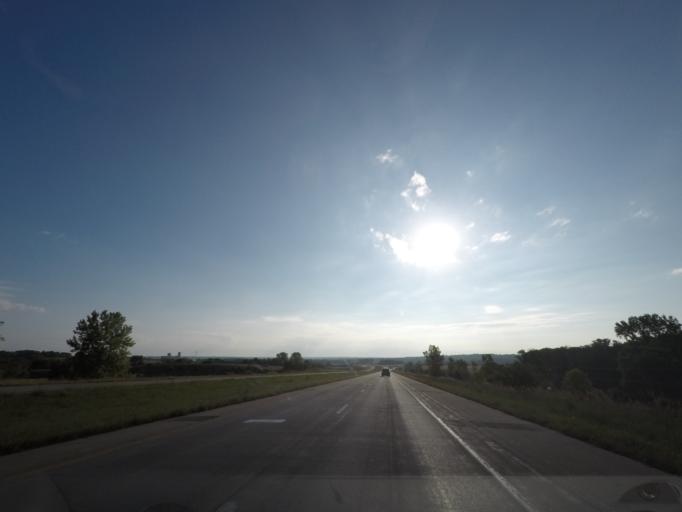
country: US
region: Iowa
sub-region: Warren County
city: Carlisle
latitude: 41.5115
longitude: -93.5384
